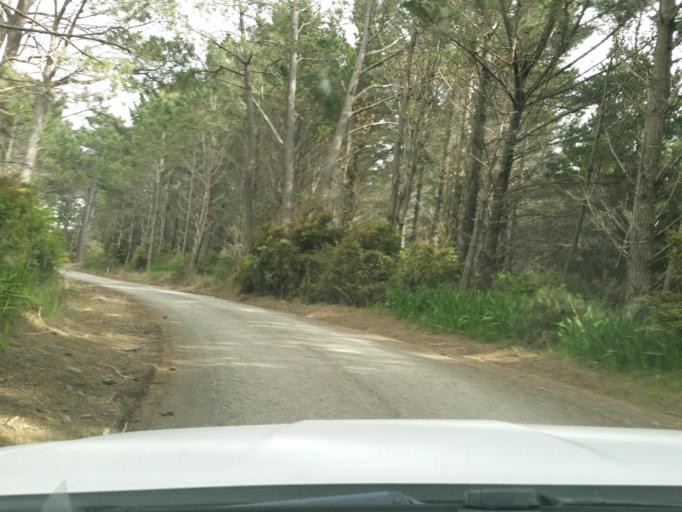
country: NZ
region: Northland
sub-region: Kaipara District
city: Dargaville
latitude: -35.7829
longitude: 173.6708
